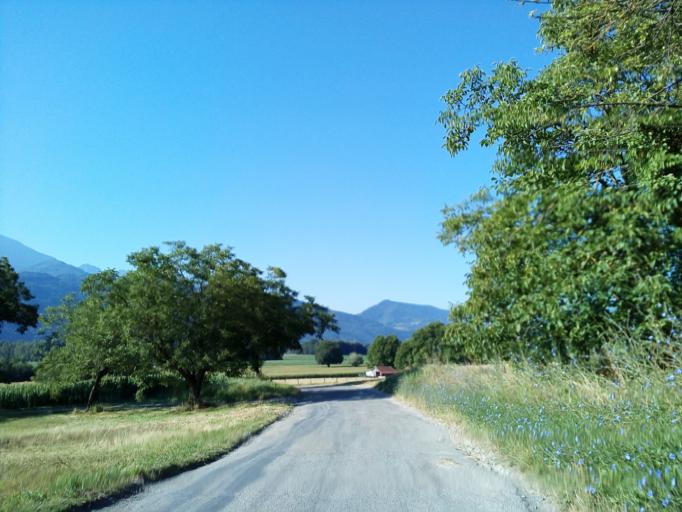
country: FR
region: Rhone-Alpes
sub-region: Departement de l'Isere
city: Bernin
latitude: 45.2586
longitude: 5.8697
